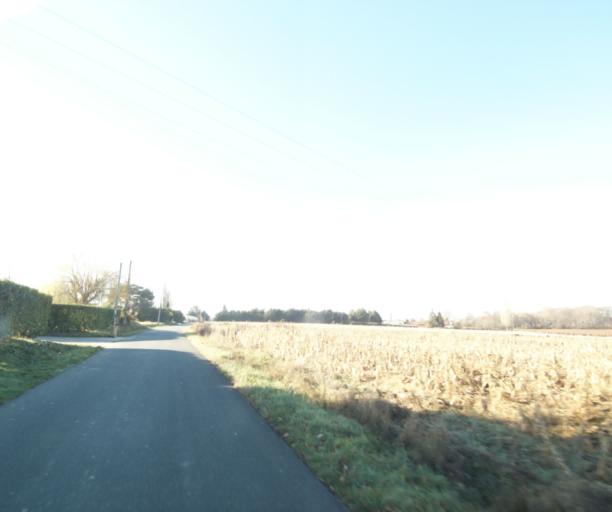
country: FR
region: Poitou-Charentes
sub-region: Departement de la Charente-Maritime
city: Fontcouverte
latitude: 45.7505
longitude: -0.5704
